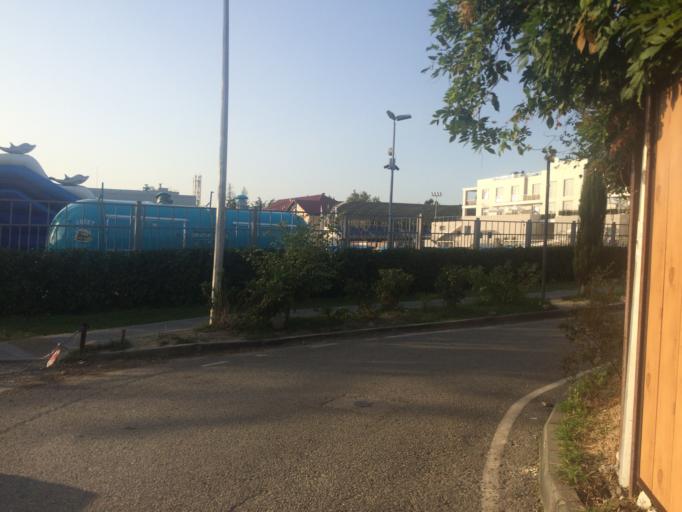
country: RU
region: Krasnodarskiy
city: Adler
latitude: 43.3885
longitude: 39.9861
